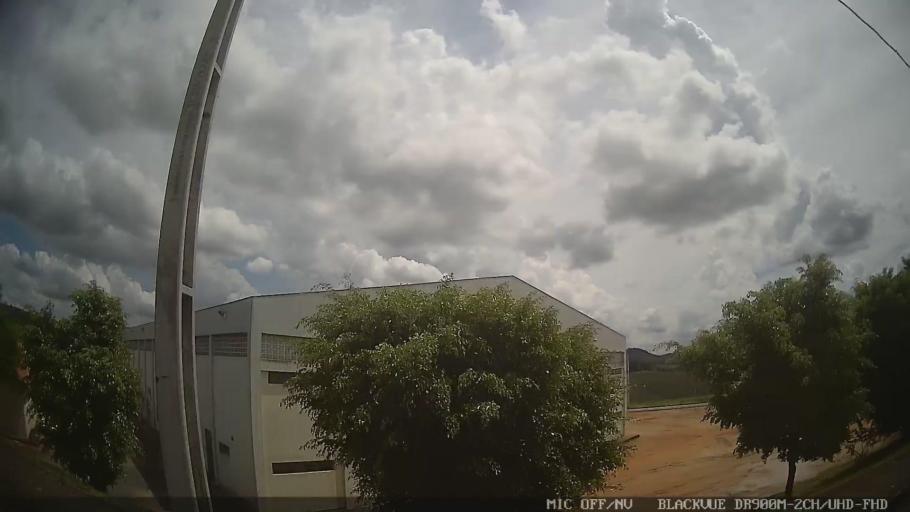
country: BR
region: Minas Gerais
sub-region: Extrema
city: Extrema
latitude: -22.7416
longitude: -46.3781
